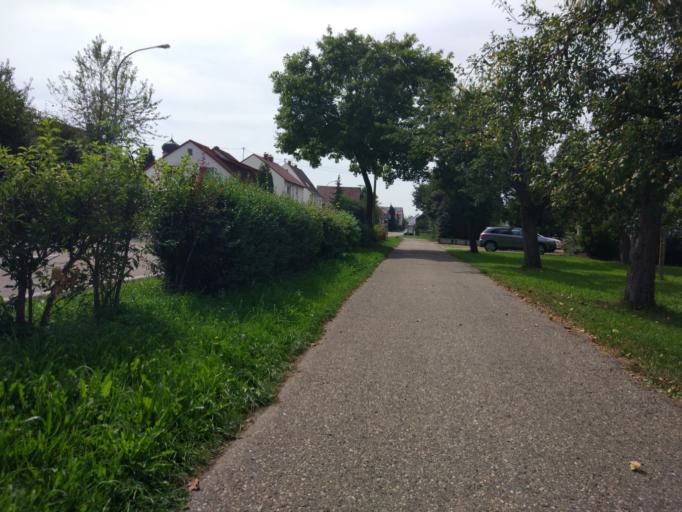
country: DE
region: Baden-Wuerttemberg
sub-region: Tuebingen Region
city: Ersingen
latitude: 48.2946
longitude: 9.8561
